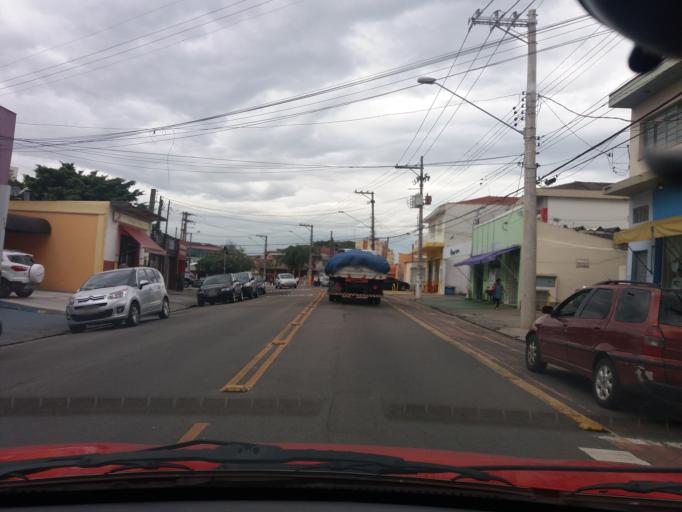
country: BR
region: Sao Paulo
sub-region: Osasco
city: Osasco
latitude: -23.5763
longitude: -46.7447
